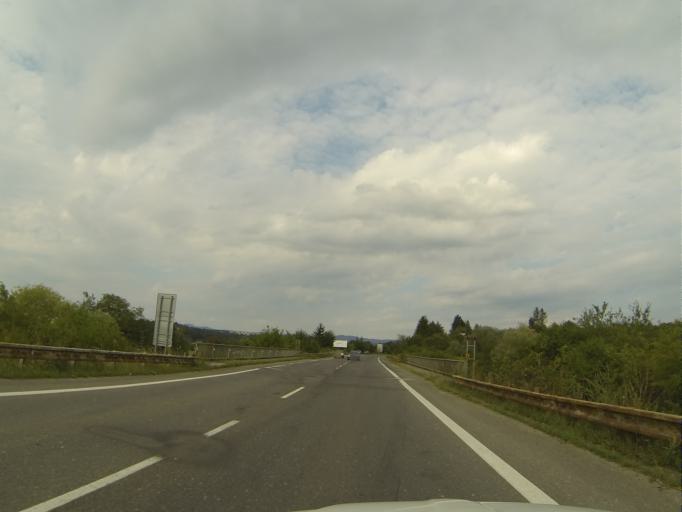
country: SK
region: Nitriansky
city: Prievidza
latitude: 48.7630
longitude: 18.6311
